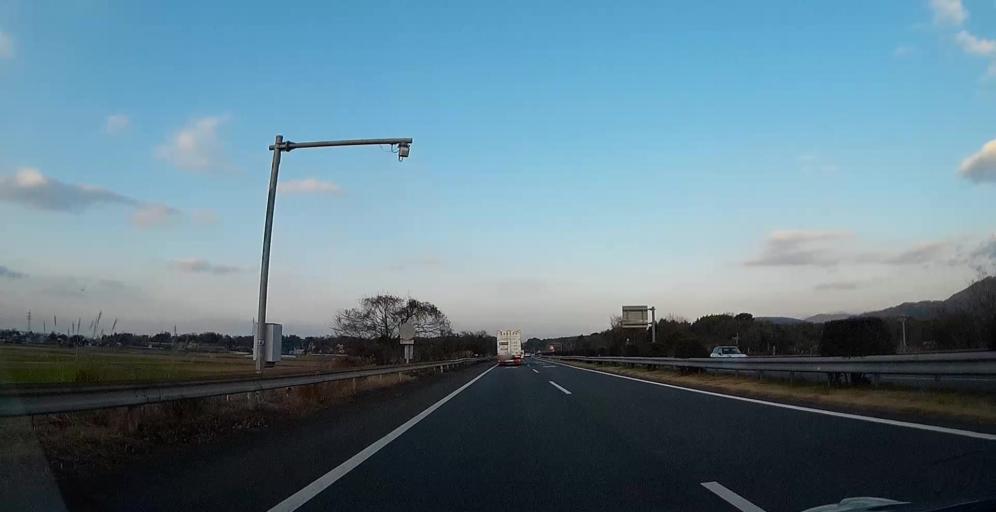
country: JP
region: Kumamoto
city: Kumamoto
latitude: 32.7361
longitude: 130.7786
